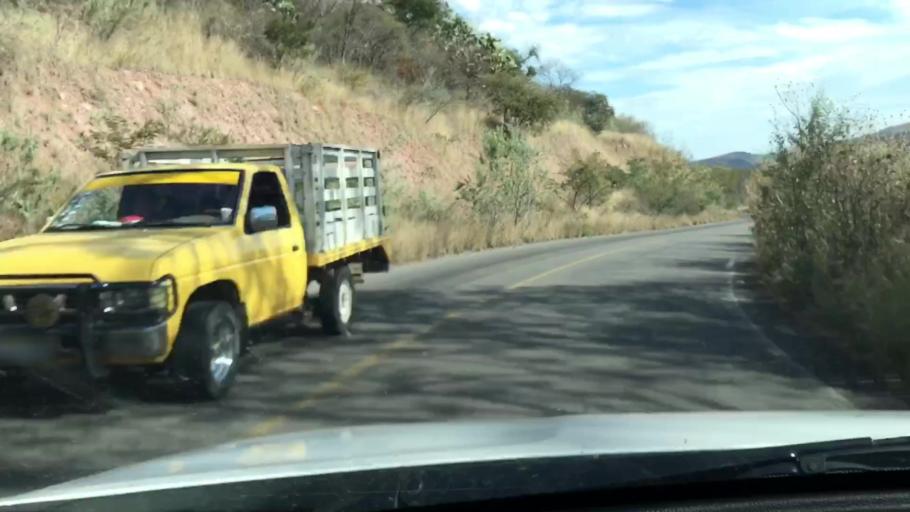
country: MX
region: Jalisco
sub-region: Zacoalco de Torres
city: Barranca de Otates (Barranca de Otatan)
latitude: 20.2458
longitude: -103.6723
